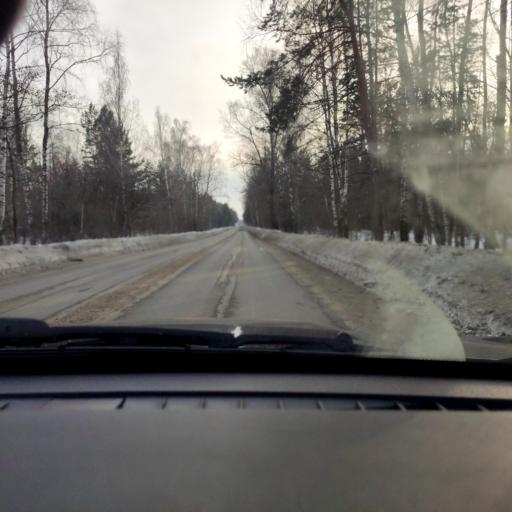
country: RU
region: Samara
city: Pribrezhnyy
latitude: 53.5083
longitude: 49.8501
